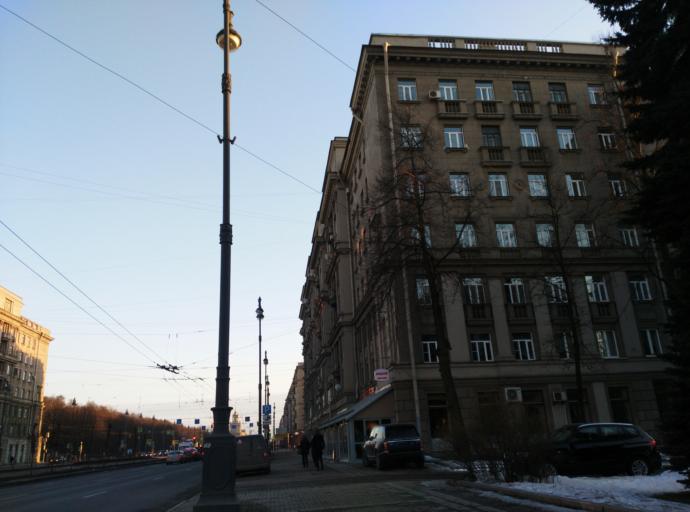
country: RU
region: St.-Petersburg
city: Kupchino
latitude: 59.8731
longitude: 30.3198
